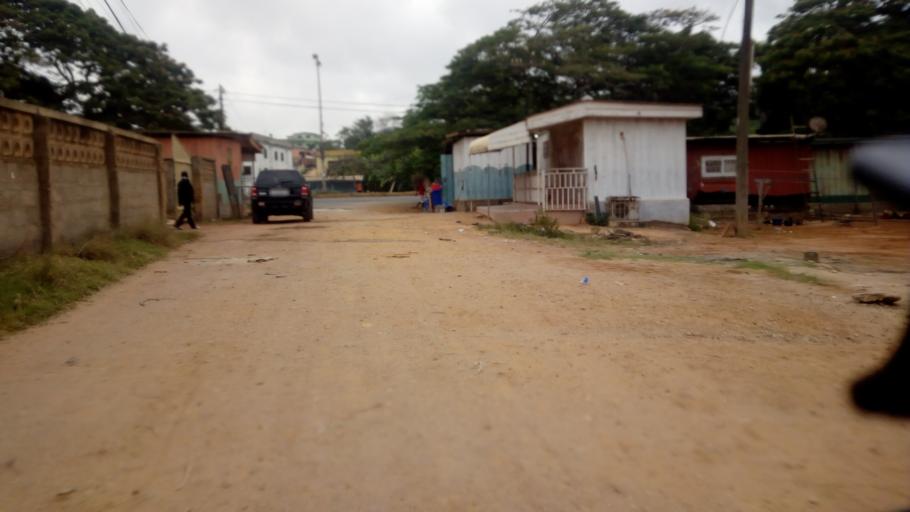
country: GH
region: Central
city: Cape Coast
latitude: 5.1202
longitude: -1.2682
